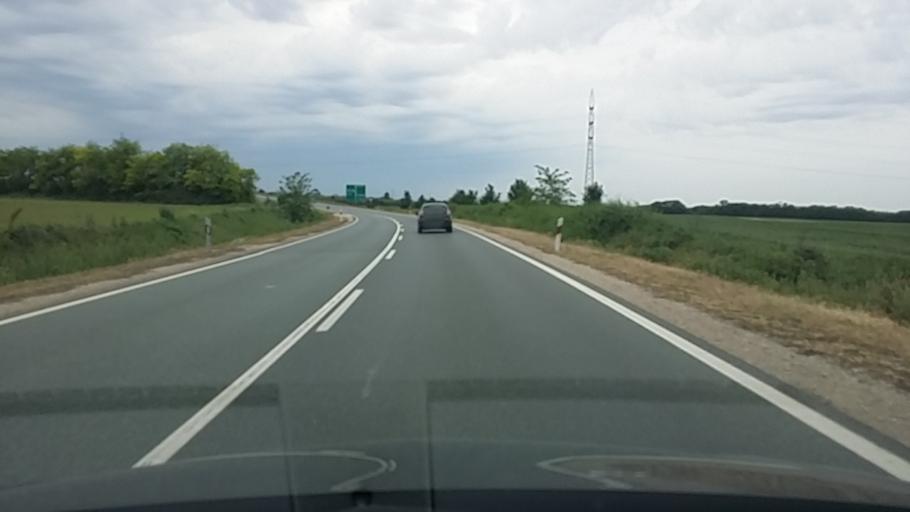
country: HU
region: Fejer
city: dunaujvaros
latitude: 46.9914
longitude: 18.8938
